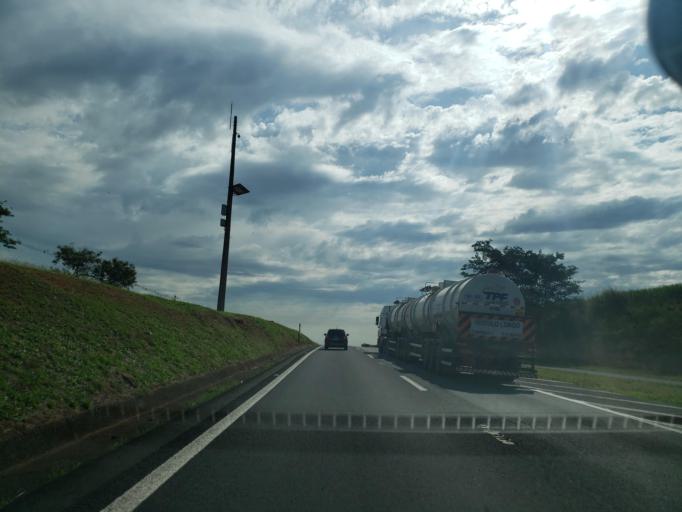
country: BR
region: Sao Paulo
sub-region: Cafelandia
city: Cafelandia
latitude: -21.8733
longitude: -49.5631
